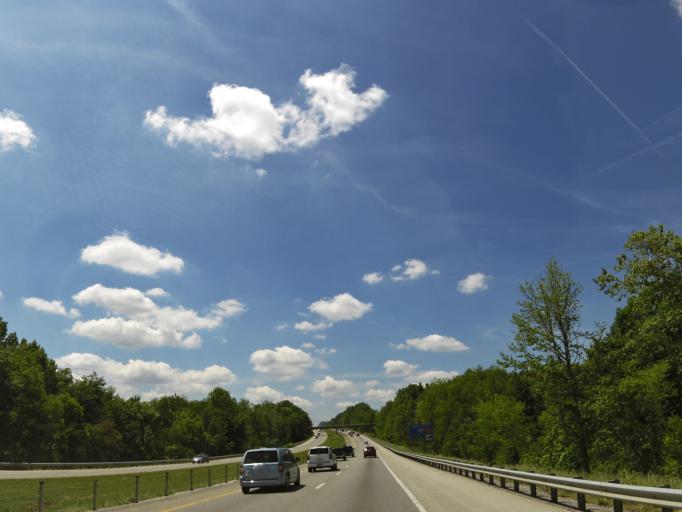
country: US
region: Kentucky
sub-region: Whitley County
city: Corbin
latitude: 36.9487
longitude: -84.1220
